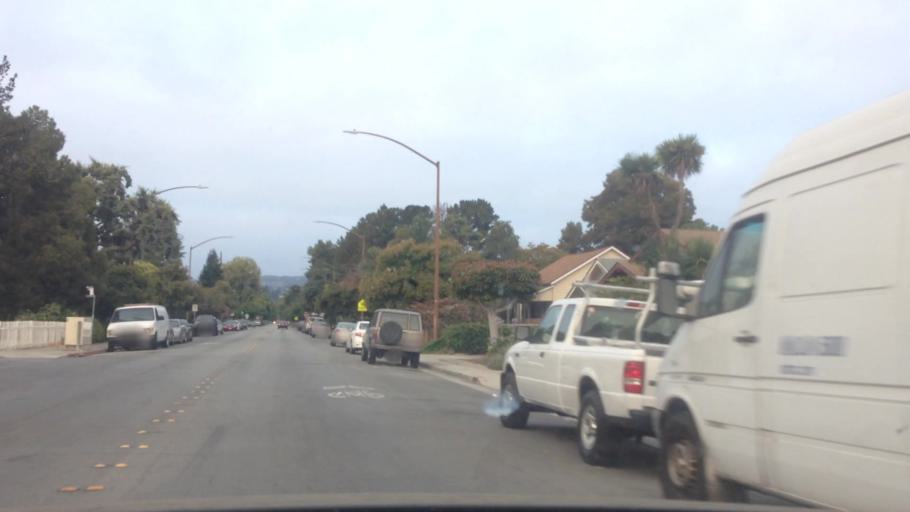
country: US
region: California
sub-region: San Mateo County
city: Redwood City
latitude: 37.4752
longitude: -122.2306
